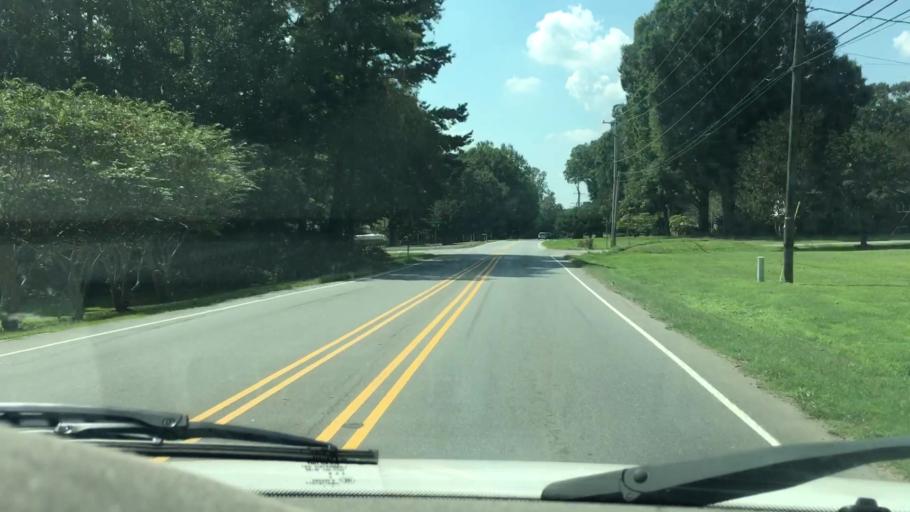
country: US
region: North Carolina
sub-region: Mecklenburg County
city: Huntersville
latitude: 35.3565
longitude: -80.8706
